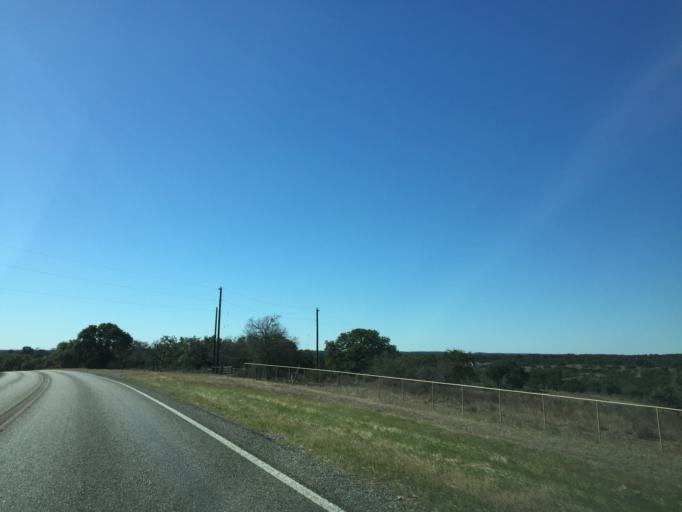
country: US
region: Texas
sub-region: Comal County
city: Canyon Lake
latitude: 29.7602
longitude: -98.3056
